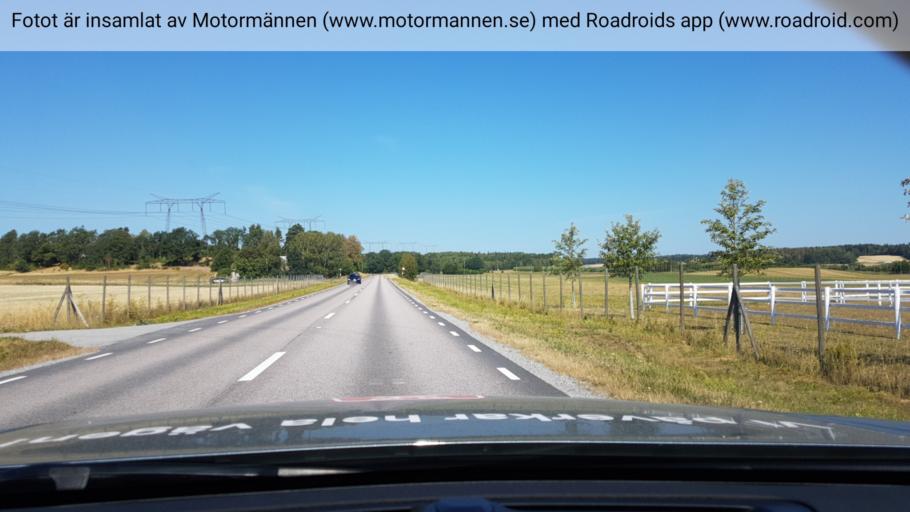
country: SE
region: Stockholm
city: Stenhamra
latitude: 59.3441
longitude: 17.6338
